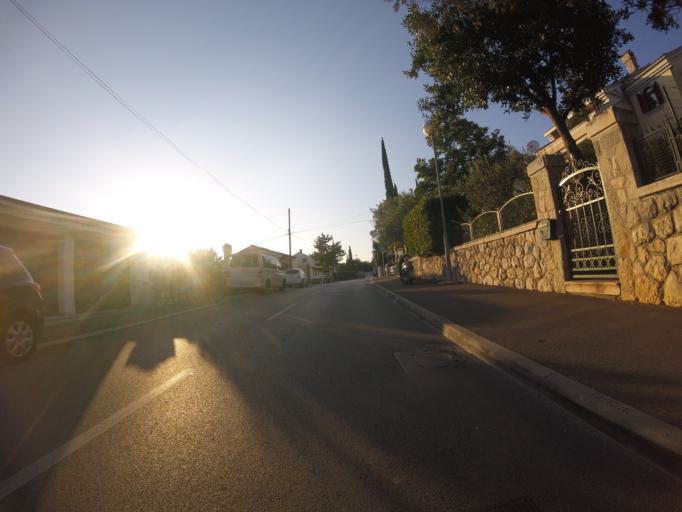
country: HR
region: Primorsko-Goranska
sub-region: Grad Crikvenica
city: Crikvenica
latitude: 45.1954
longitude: 14.6642
